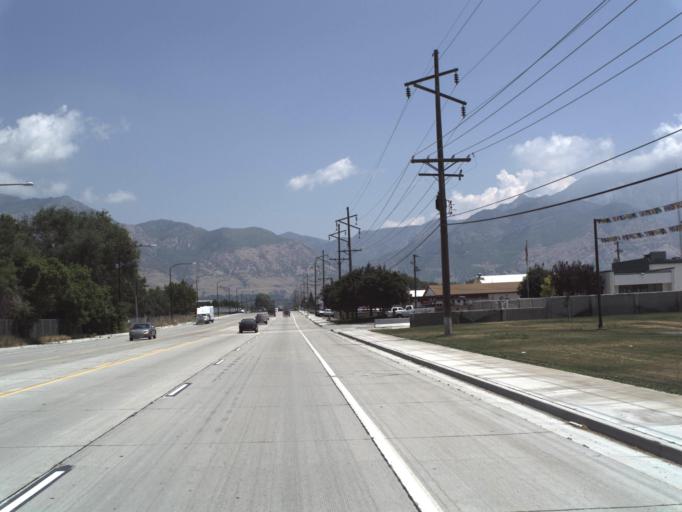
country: US
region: Utah
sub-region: Weber County
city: Marriott-Slaterville
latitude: 41.2445
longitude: -112.0032
